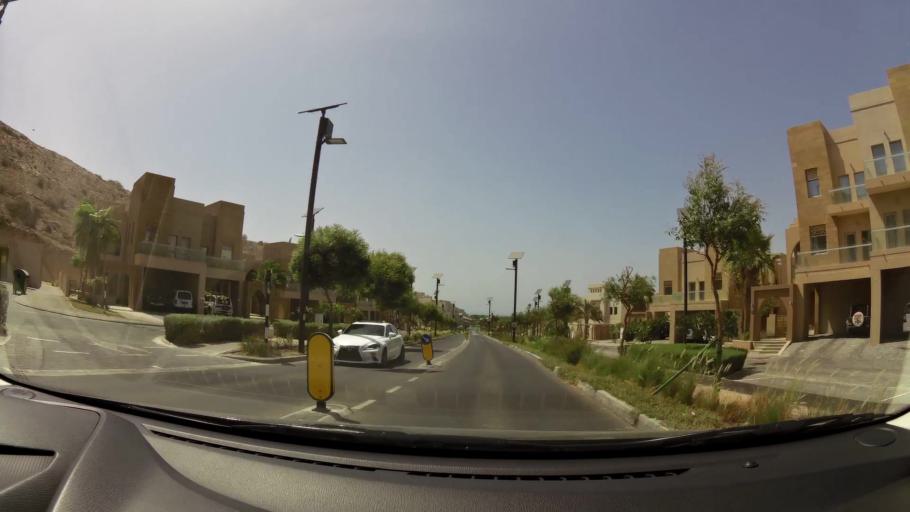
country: OM
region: Muhafazat Masqat
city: Muscat
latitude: 23.6302
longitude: 58.5024
